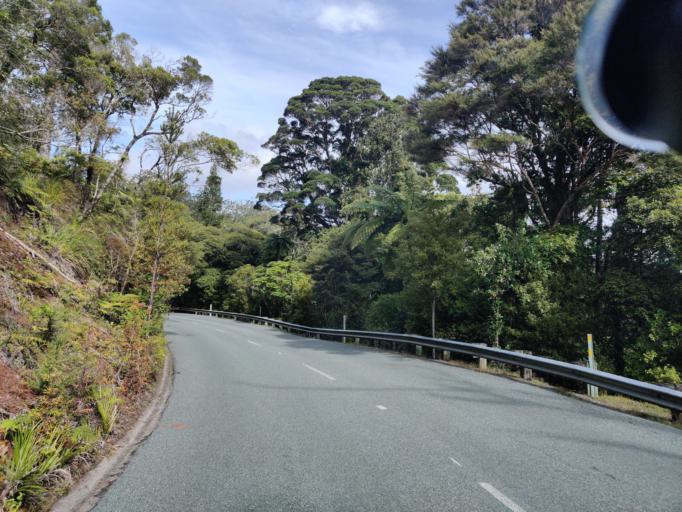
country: NZ
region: Northland
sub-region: Kaipara District
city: Dargaville
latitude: -35.6466
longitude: 173.5577
